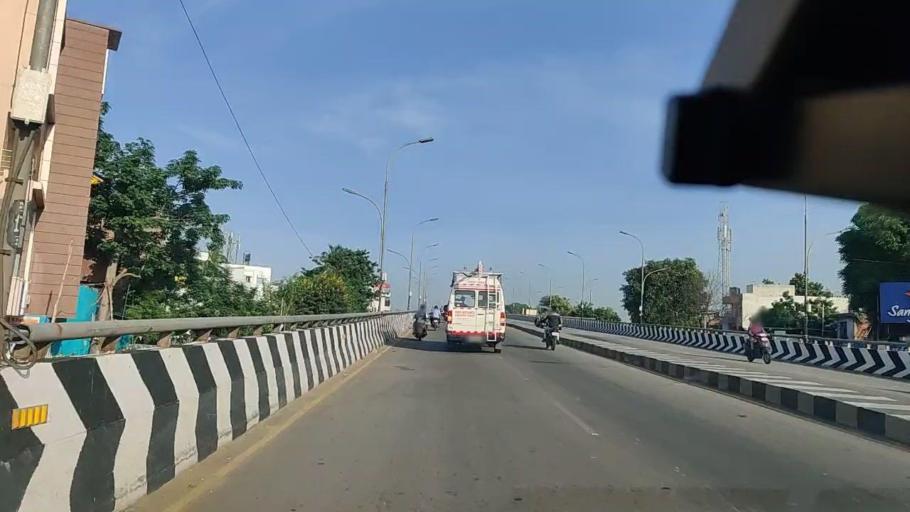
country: IN
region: Tamil Nadu
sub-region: Thiruvallur
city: Chinnasekkadu
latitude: 13.1275
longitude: 80.2434
